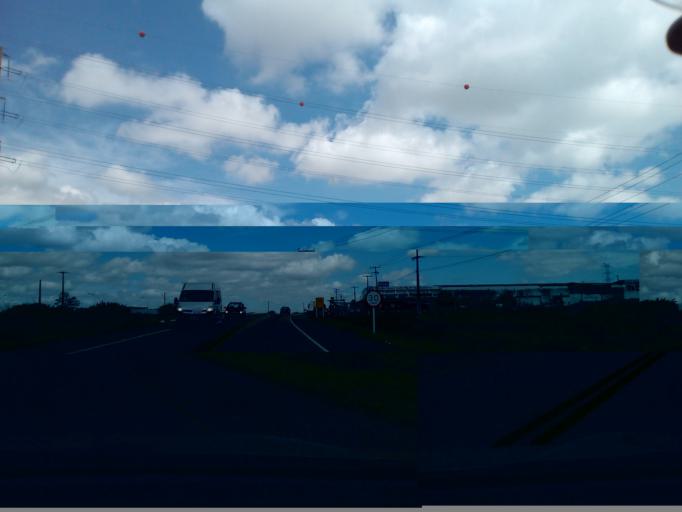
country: BR
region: Paraiba
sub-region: Campina Grande
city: Campina Grande
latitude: -7.2788
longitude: -35.8946
